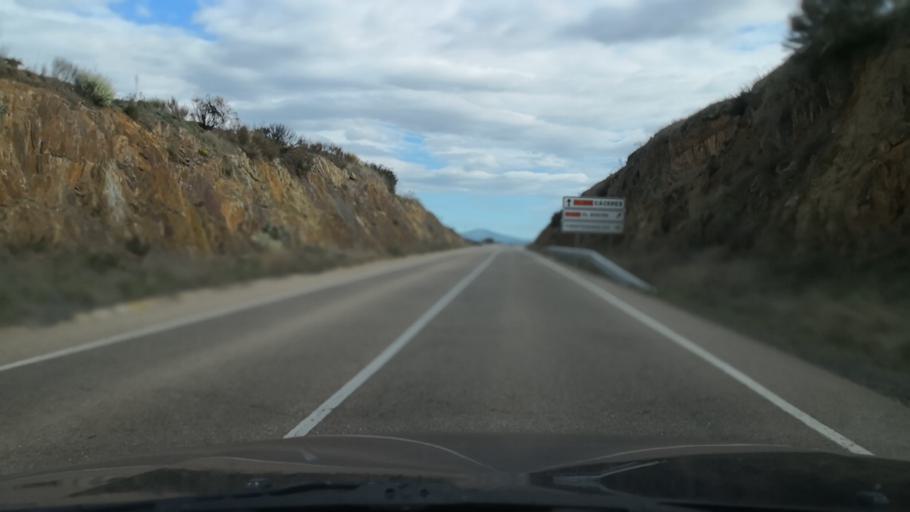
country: ES
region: Castille and Leon
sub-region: Provincia de Salamanca
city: Herguijuela de Ciudad Rodrigo
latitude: 40.4842
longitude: -6.5814
